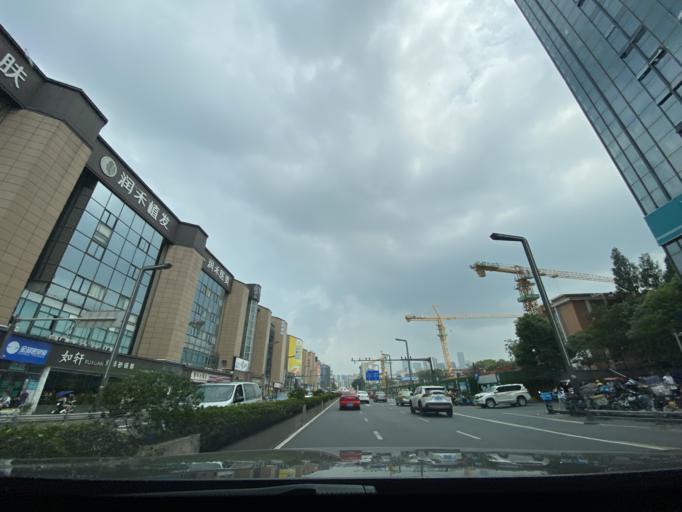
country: CN
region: Sichuan
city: Chengdu
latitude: 30.6326
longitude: 104.0739
